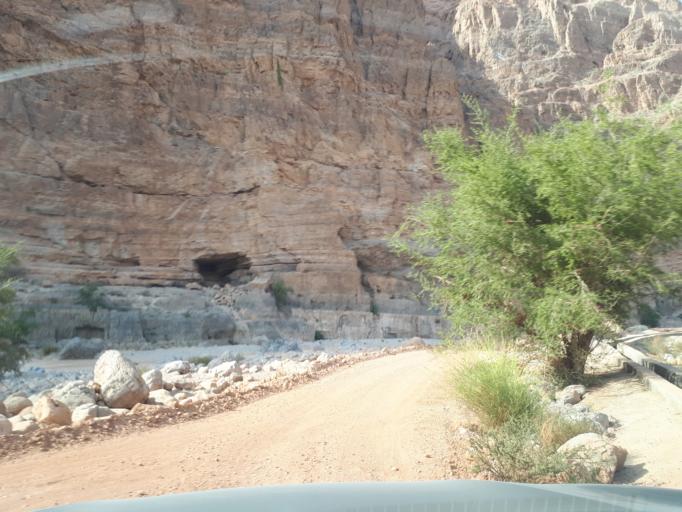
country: OM
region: Ash Sharqiyah
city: Al Qabil
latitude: 23.0701
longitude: 58.9868
